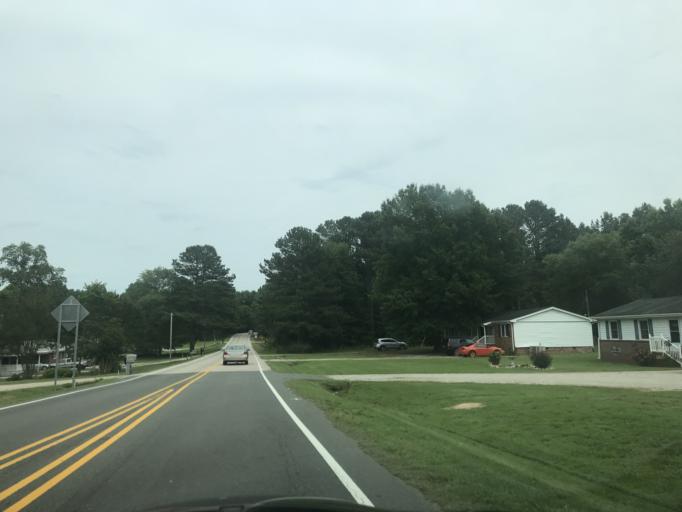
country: US
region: North Carolina
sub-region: Wake County
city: Rolesville
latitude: 35.9253
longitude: -78.5026
